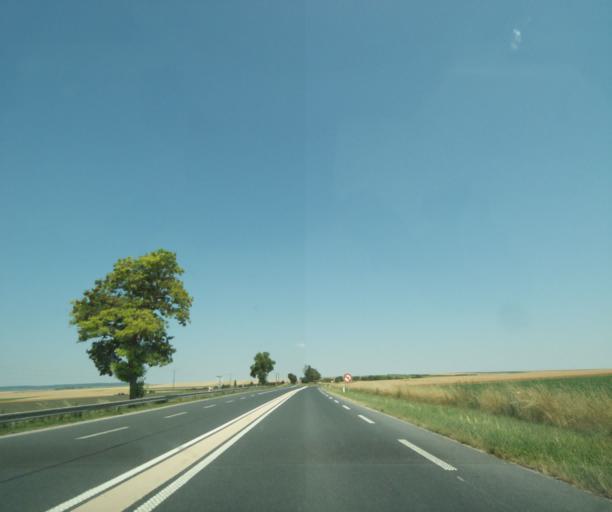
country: FR
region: Champagne-Ardenne
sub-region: Departement de la Marne
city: Fagnieres
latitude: 49.0581
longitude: 4.2986
